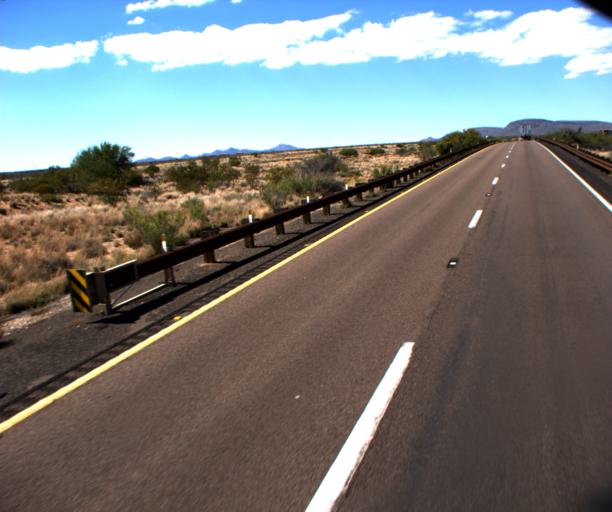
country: US
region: Arizona
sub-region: Mohave County
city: Kingman
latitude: 35.0965
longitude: -113.6657
